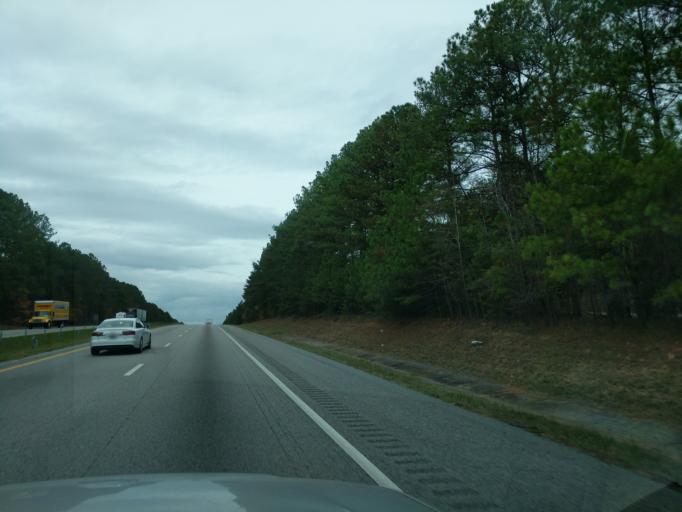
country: US
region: South Carolina
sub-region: Laurens County
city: Clinton
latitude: 34.5730
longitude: -81.8926
